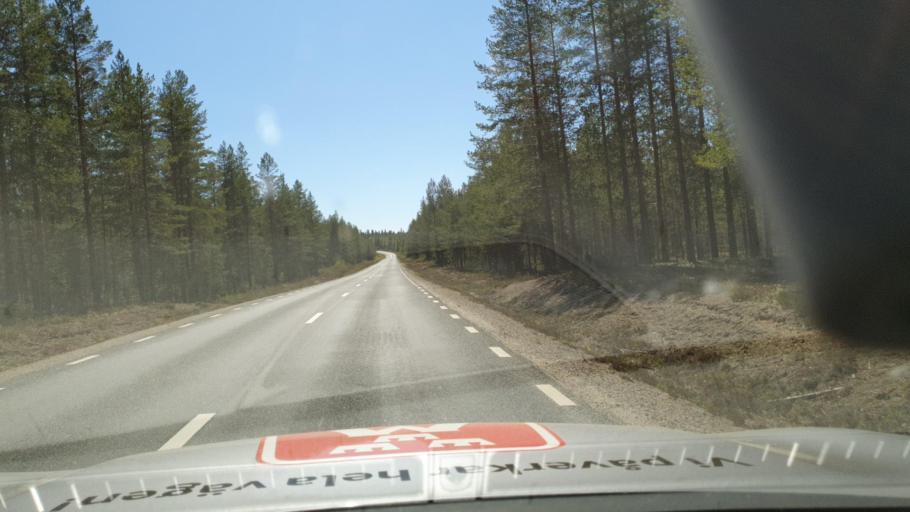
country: SE
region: Vaesternorrland
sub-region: OErnskoeldsviks Kommun
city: Bredbyn
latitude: 63.7668
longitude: 18.4863
